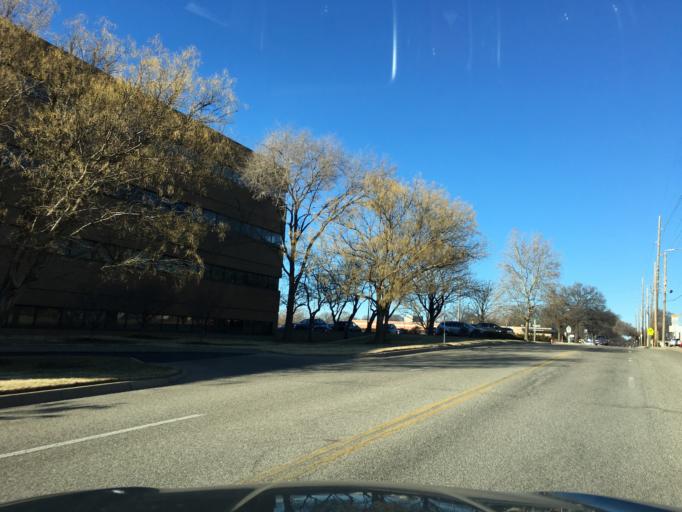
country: US
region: Kansas
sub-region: Sedgwick County
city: Wichita
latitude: 37.6656
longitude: -97.2943
